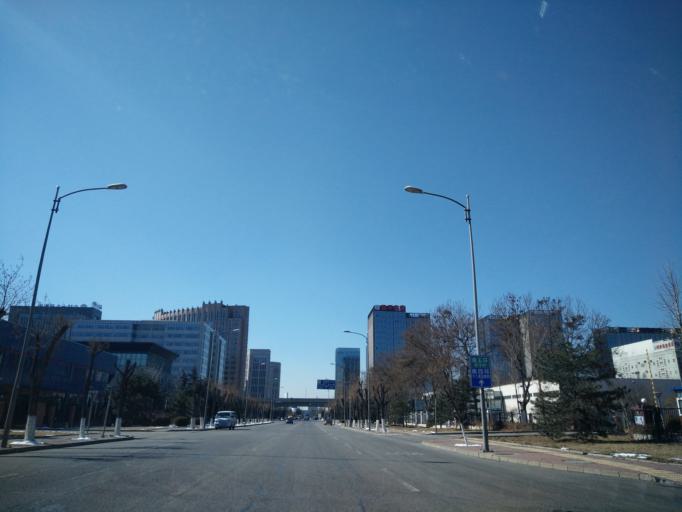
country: CN
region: Beijing
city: Jiugong
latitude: 39.7879
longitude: 116.5138
